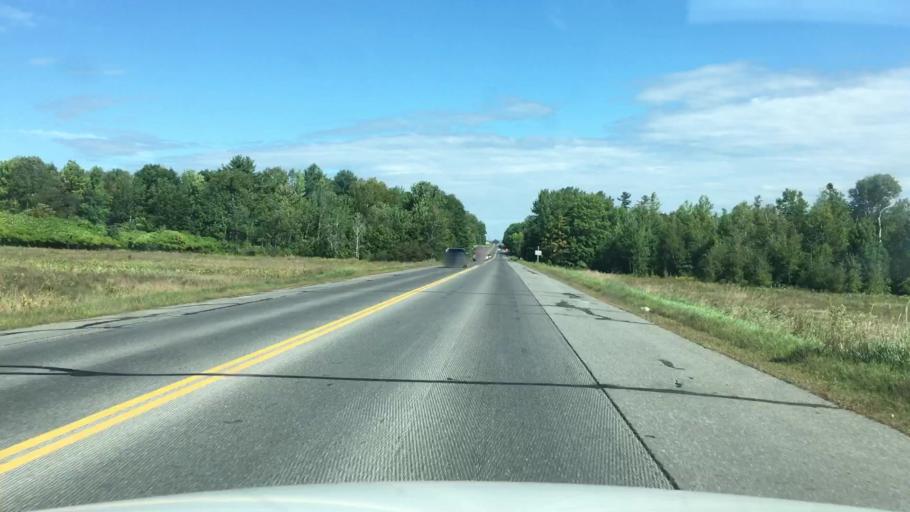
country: US
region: Maine
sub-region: Penobscot County
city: Newport
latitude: 44.8641
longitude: -69.2842
